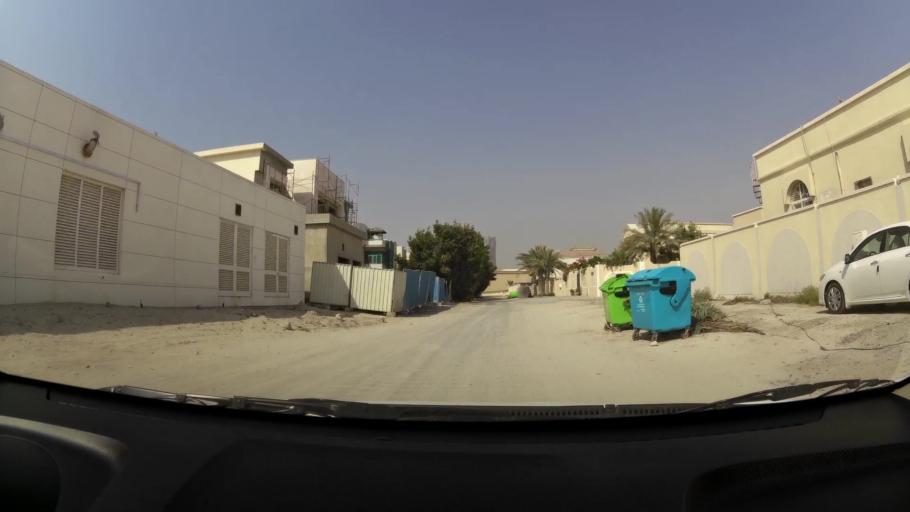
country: AE
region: Ajman
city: Ajman
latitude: 25.3877
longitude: 55.4197
